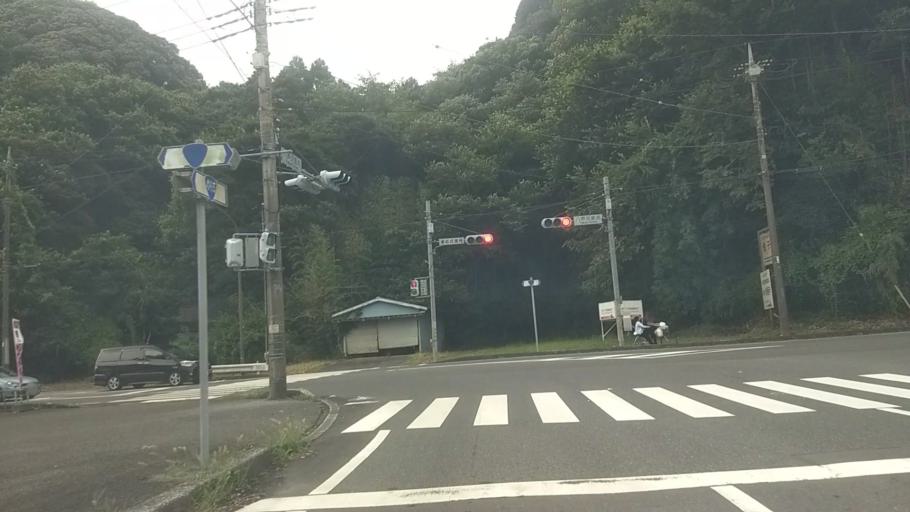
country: JP
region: Chiba
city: Ohara
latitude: 35.2709
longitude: 140.2552
